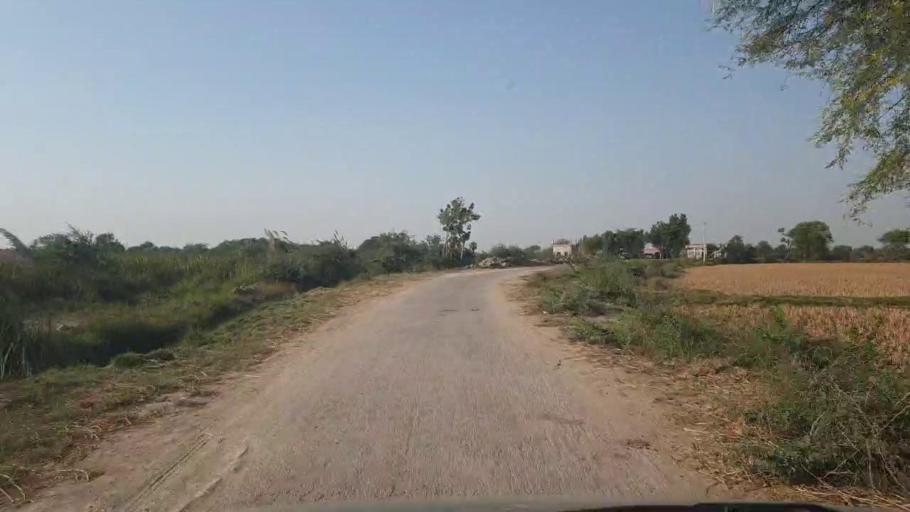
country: PK
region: Sindh
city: Badin
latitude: 24.6556
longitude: 68.8115
